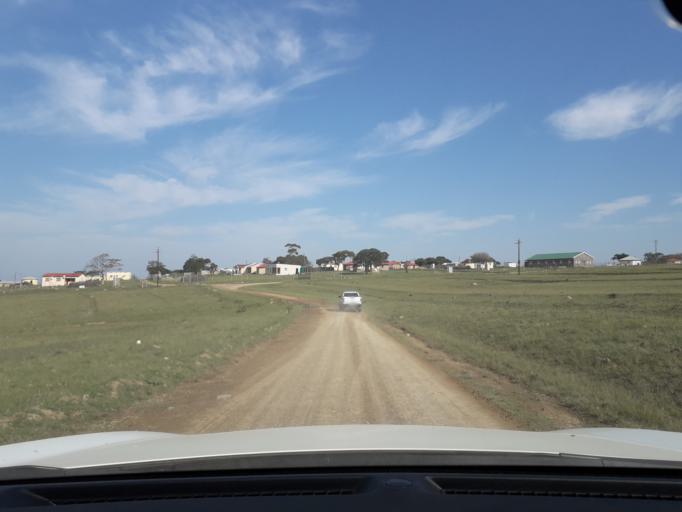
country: ZA
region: Eastern Cape
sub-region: Buffalo City Metropolitan Municipality
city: Bhisho
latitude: -33.0063
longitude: 27.3094
